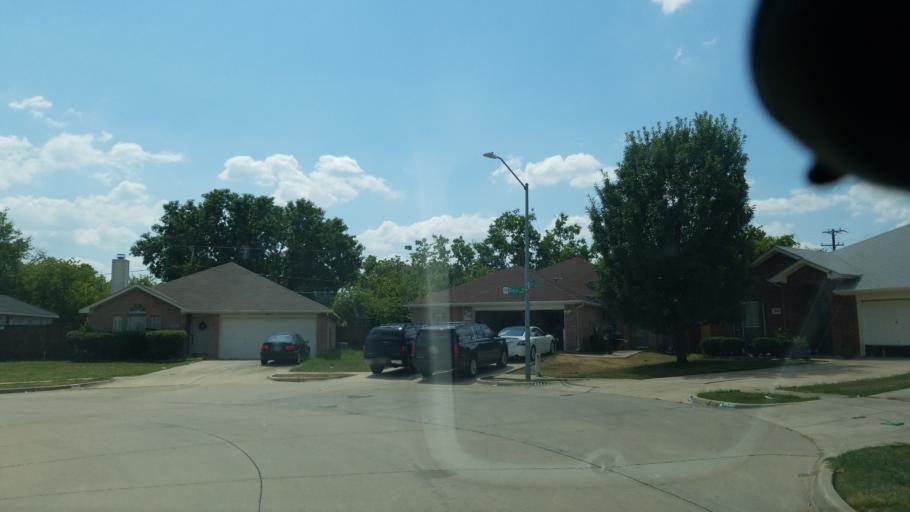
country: US
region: Texas
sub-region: Dallas County
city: Grand Prairie
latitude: 32.7065
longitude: -96.9916
